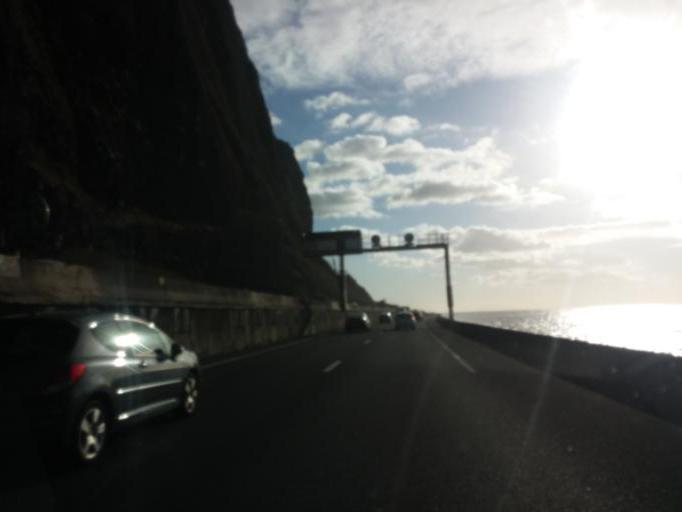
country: RE
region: Reunion
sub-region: Reunion
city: Saint-Denis
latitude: -20.8754
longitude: 55.4309
